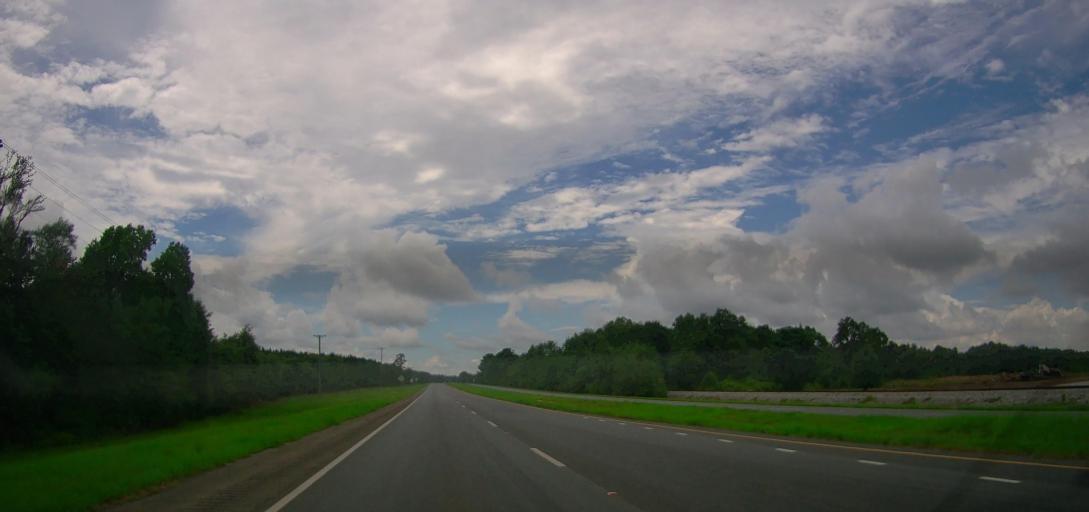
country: US
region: Georgia
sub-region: Dodge County
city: Eastman
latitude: 32.1068
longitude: -83.0773
